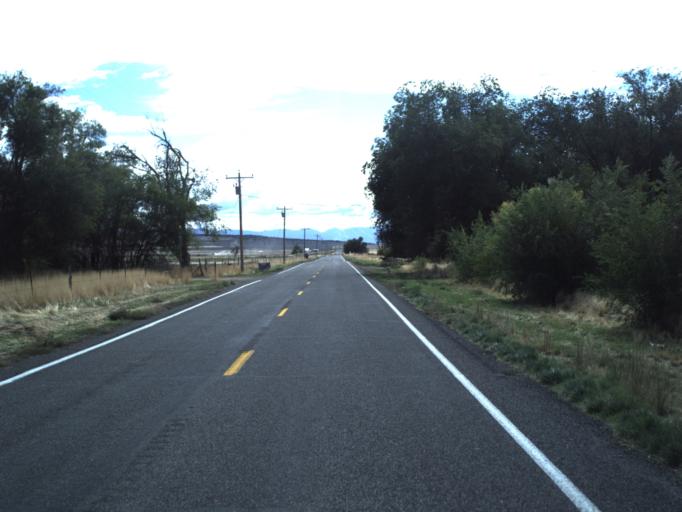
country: US
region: Utah
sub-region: Millard County
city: Fillmore
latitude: 39.0454
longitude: -112.4099
